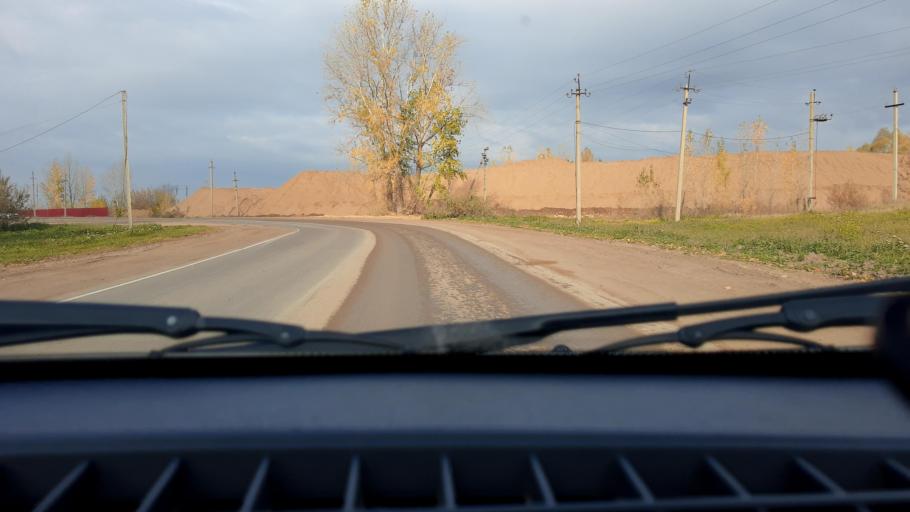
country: RU
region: Bashkortostan
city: Kabakovo
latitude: 54.5483
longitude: 56.1111
